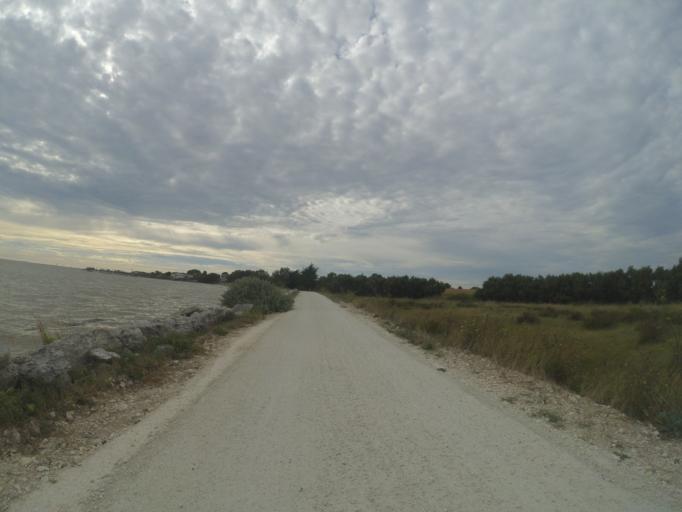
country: FR
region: Poitou-Charentes
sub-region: Departement de la Charente-Maritime
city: Meschers-sur-Gironde
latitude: 45.5509
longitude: -0.9174
